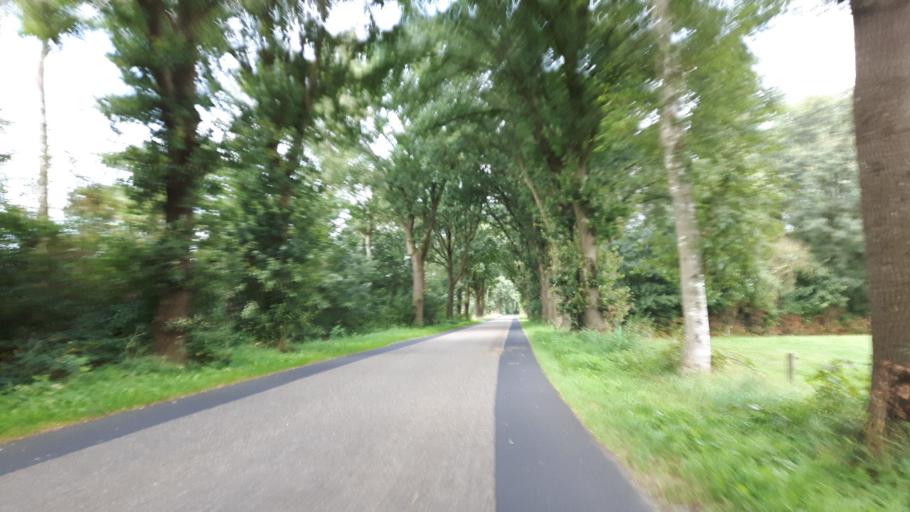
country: NL
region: Groningen
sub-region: Gemeente Leek
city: Leek
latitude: 53.0850
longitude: 6.3200
